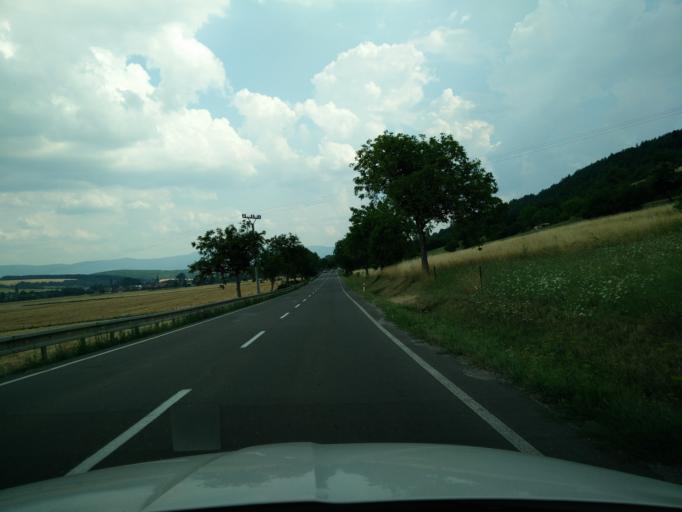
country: SK
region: Nitriansky
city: Novaky
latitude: 48.7884
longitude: 18.4794
